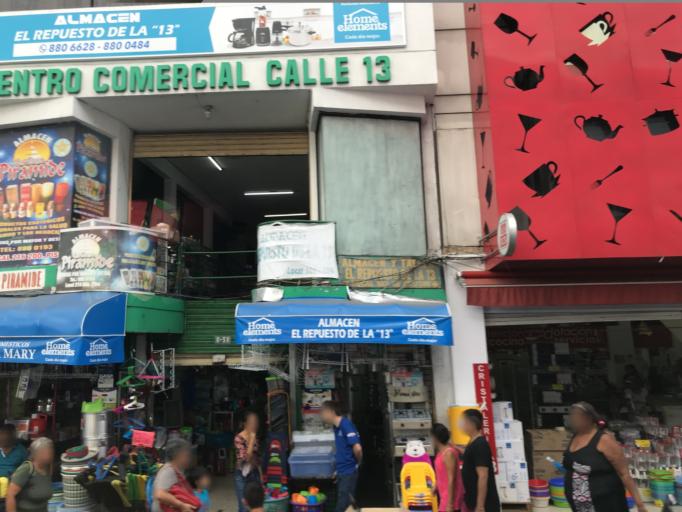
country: CO
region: Valle del Cauca
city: Cali
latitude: 3.4489
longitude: -76.5303
